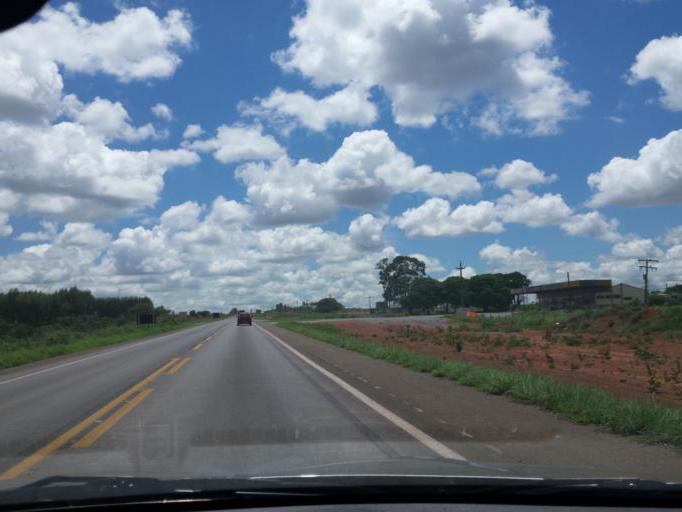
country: BR
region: Goias
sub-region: Cristalina
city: Cristalina
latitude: -16.7144
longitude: -47.6671
